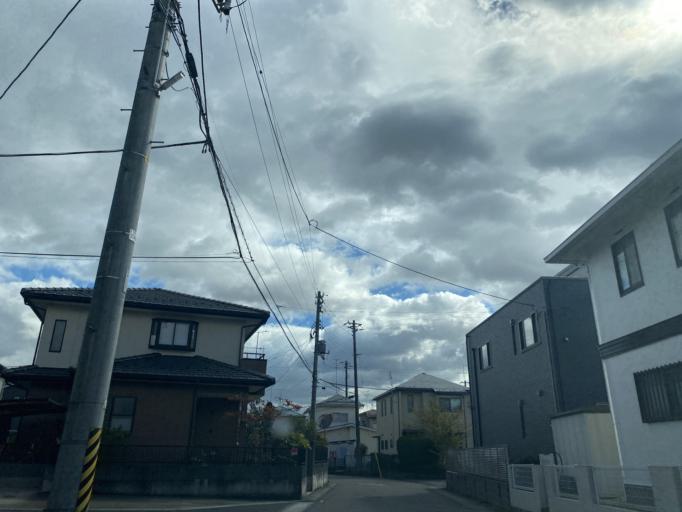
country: JP
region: Fukushima
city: Koriyama
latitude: 37.3831
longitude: 140.3409
